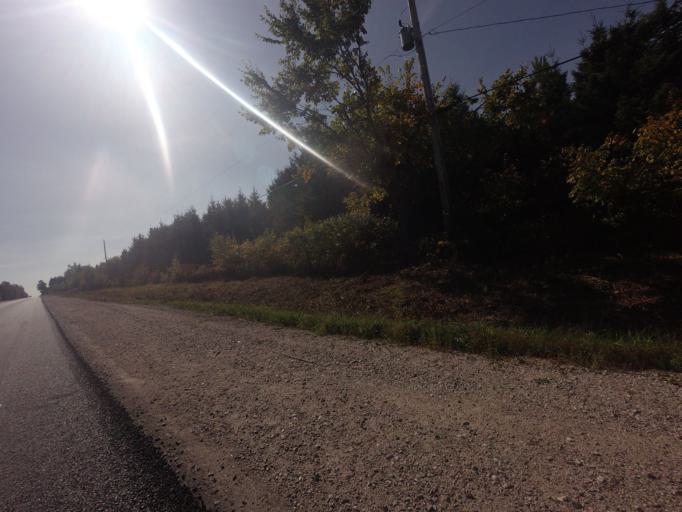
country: CA
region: Quebec
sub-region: Outaouais
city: Maniwaki
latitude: 46.5400
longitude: -75.8239
